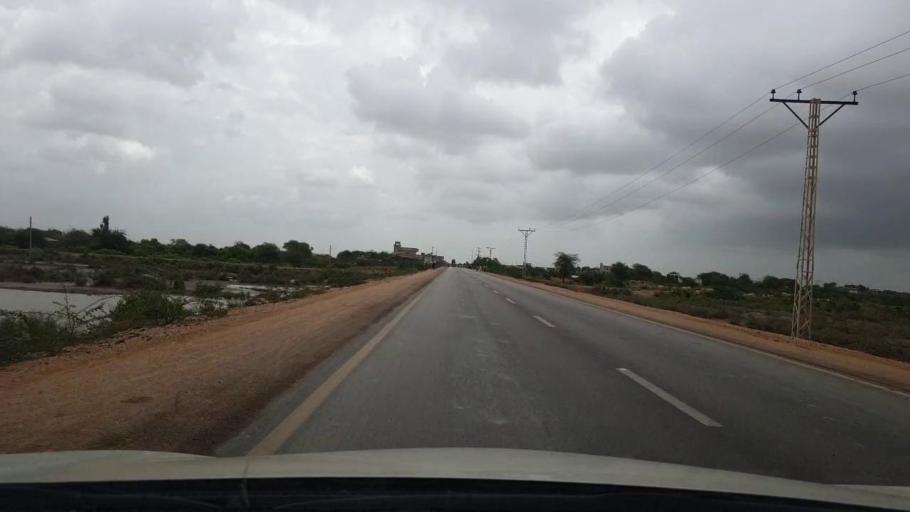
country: PK
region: Sindh
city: Mirpur Batoro
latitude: 24.6435
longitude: 68.4067
